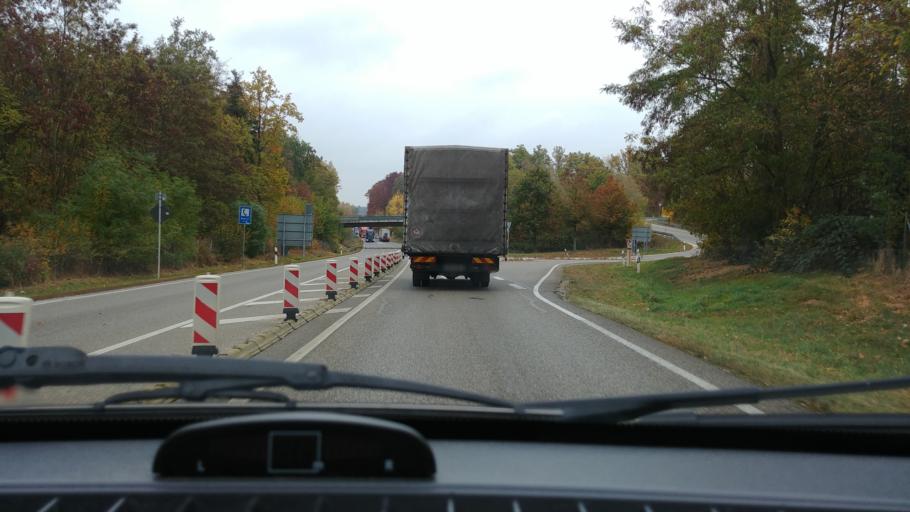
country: DE
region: Baden-Wuerttemberg
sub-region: Regierungsbezirk Stuttgart
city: Aalen
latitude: 48.8612
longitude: 10.0742
